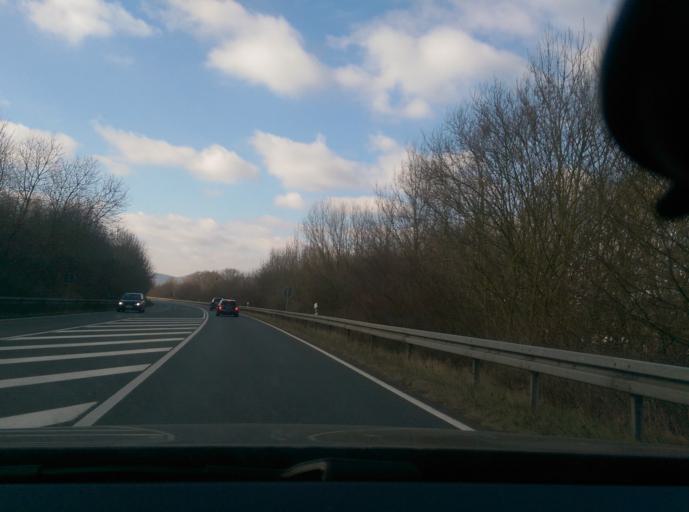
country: DE
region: Lower Saxony
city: Hessisch Oldendorf
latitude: 52.1608
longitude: 9.2700
